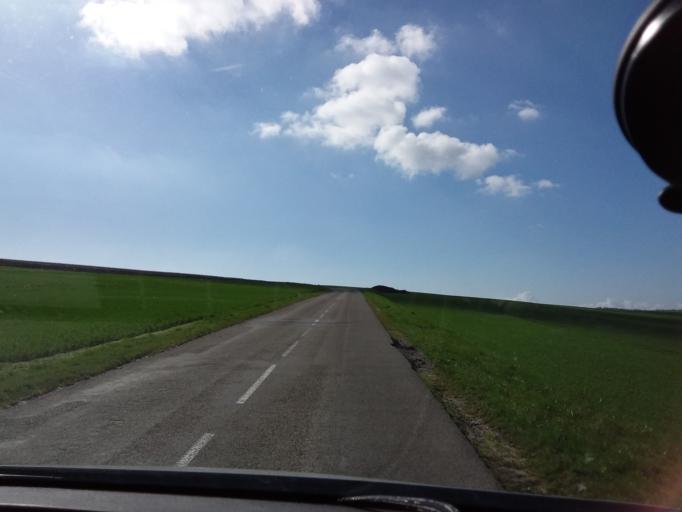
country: FR
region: Picardie
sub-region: Departement de l'Aisne
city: Origny-en-Thierache
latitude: 49.7949
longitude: 4.0093
